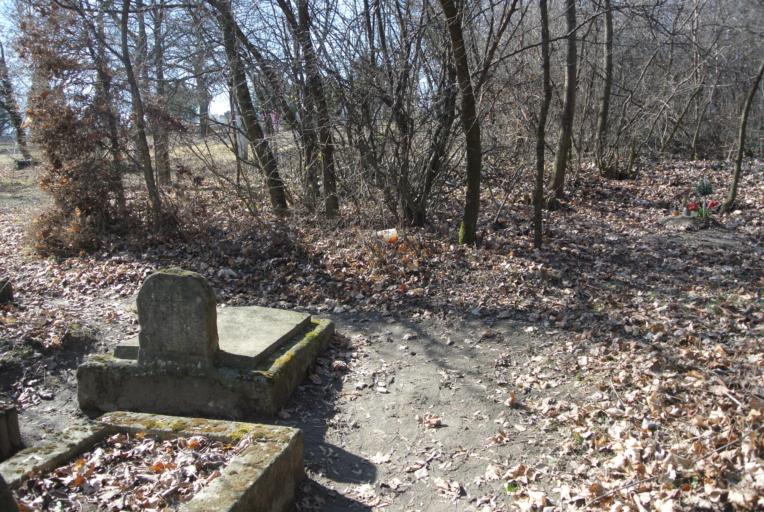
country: HU
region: Pest
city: Soskut
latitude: 47.4024
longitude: 18.7780
